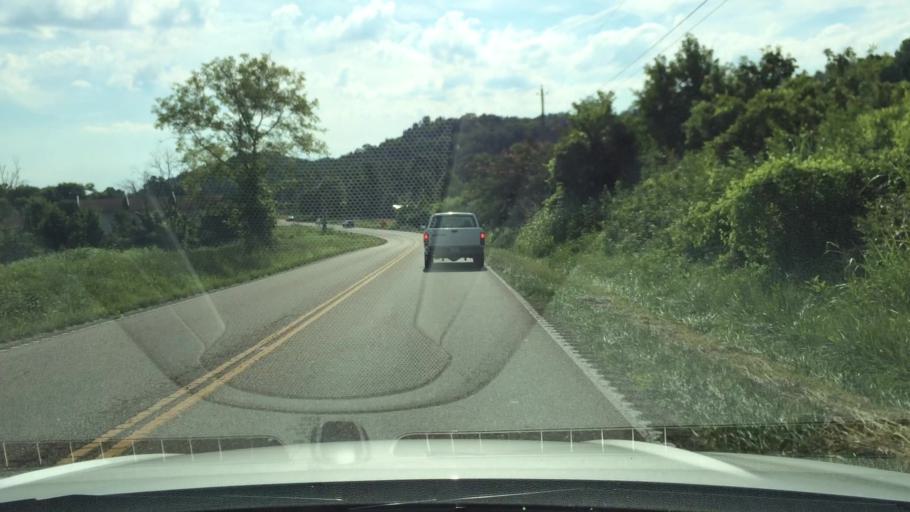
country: US
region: Tennessee
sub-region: Sevier County
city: Sevierville
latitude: 35.9138
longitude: -83.6271
